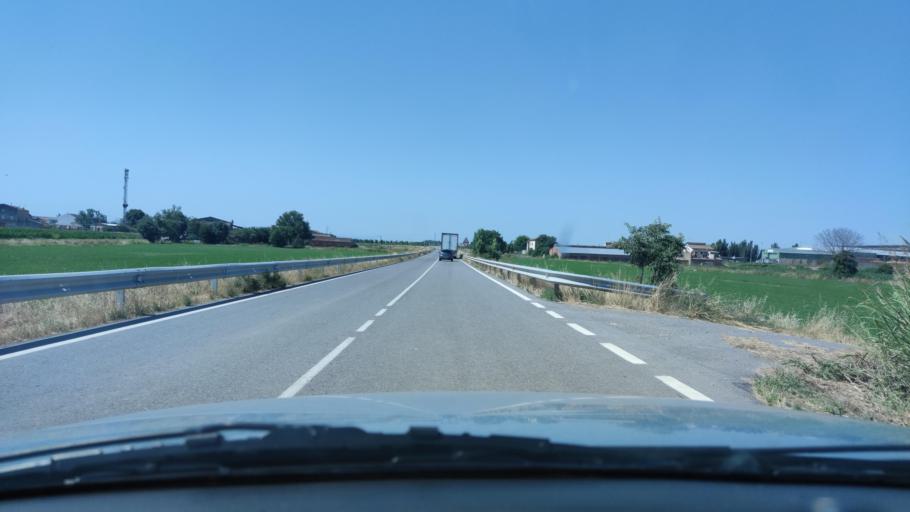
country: ES
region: Catalonia
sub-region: Provincia de Lleida
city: Ivars d'Urgell
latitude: 41.6869
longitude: 0.9832
